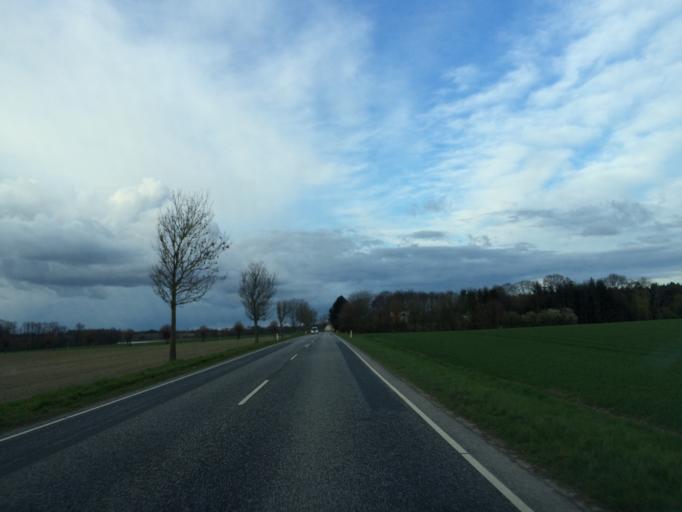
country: DK
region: South Denmark
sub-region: Odense Kommune
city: Bellinge
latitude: 55.2994
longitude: 10.2920
